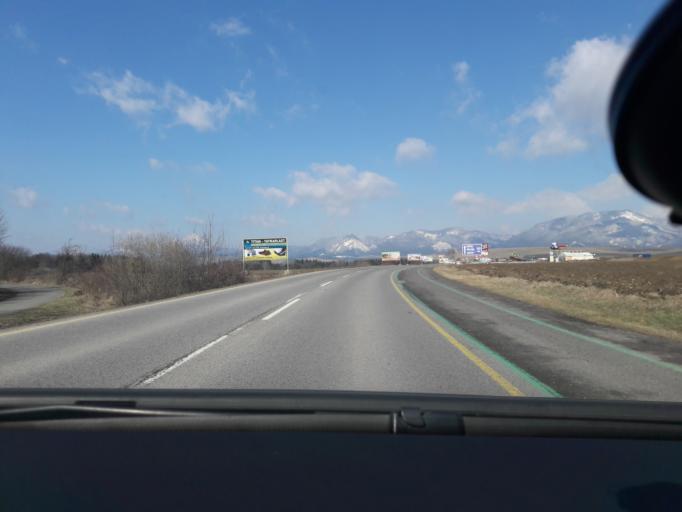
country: SK
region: Zilinsky
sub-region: Okres Liptovsky Mikulas
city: Liptovsky Mikulas
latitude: 49.0981
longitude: 19.5797
